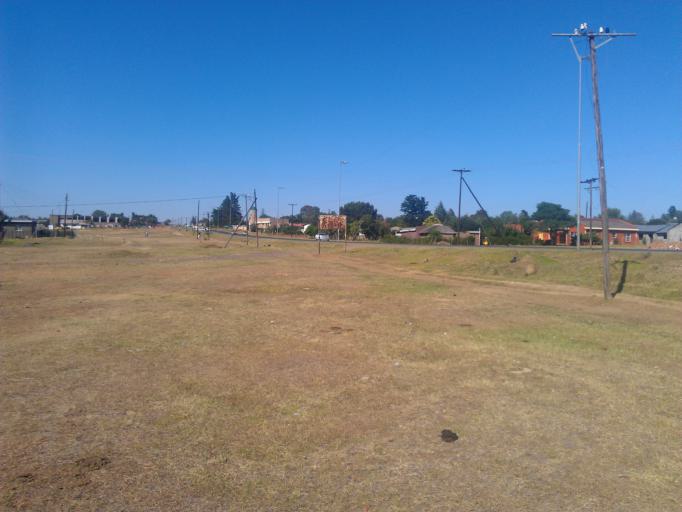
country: LS
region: Leribe
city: Leribe
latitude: -28.8613
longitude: 28.0591
